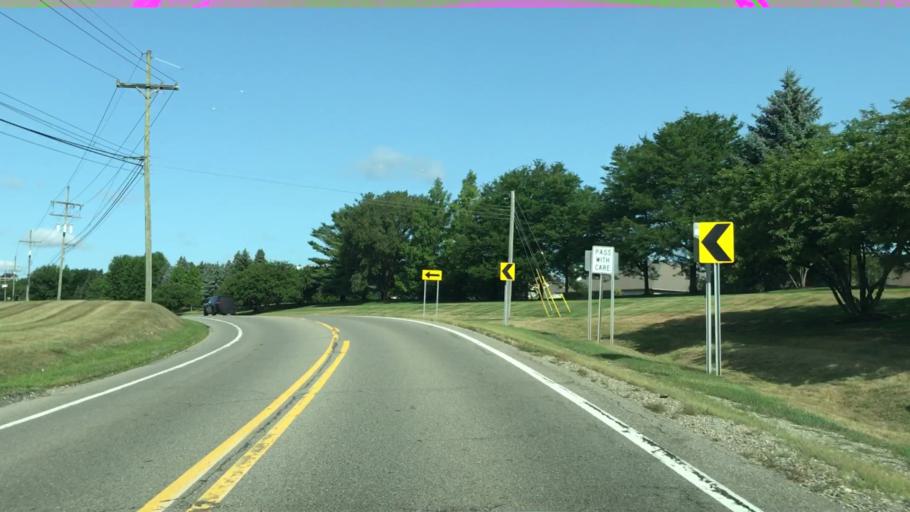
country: US
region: Michigan
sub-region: Oakland County
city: Rochester
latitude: 42.6875
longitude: -83.1112
